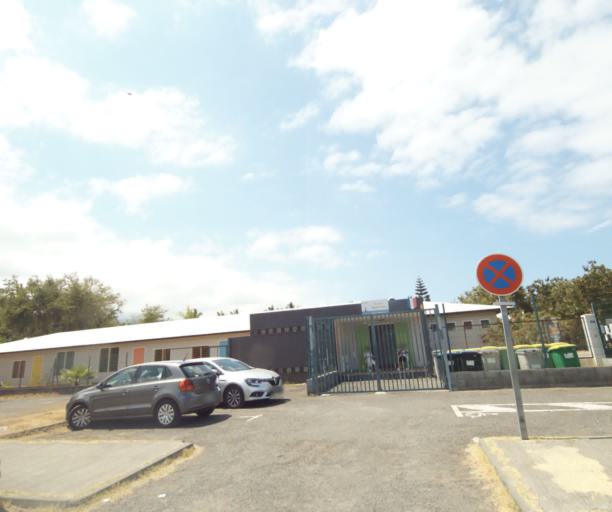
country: RE
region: Reunion
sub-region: Reunion
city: Trois-Bassins
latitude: -21.0915
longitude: 55.2367
